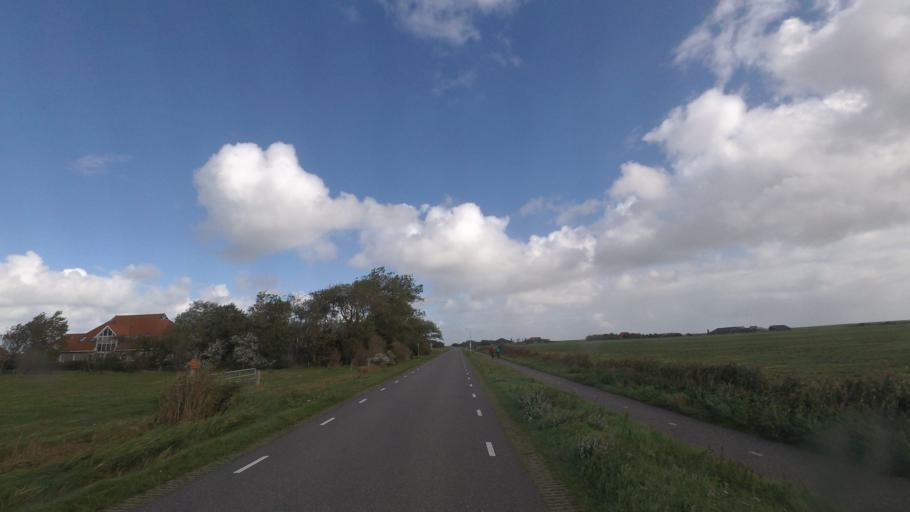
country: NL
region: Friesland
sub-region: Gemeente Ameland
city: Hollum
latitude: 53.4374
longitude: 5.6545
